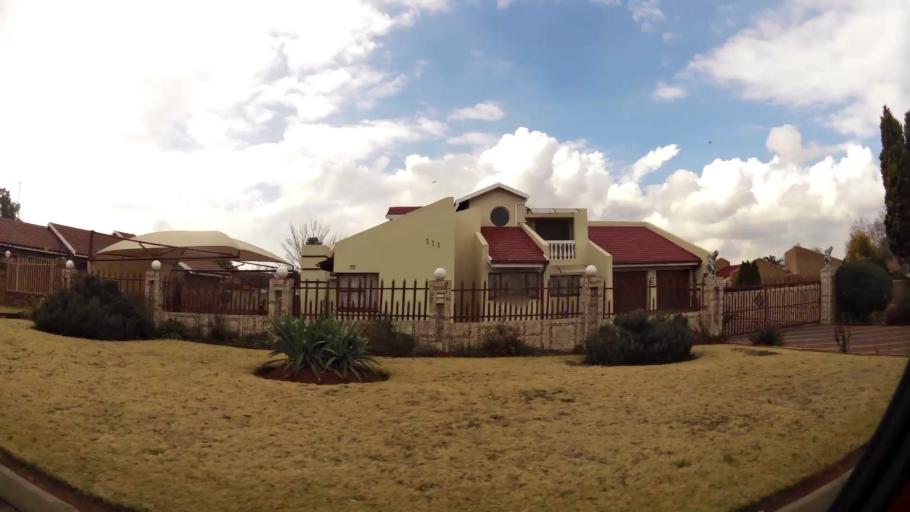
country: ZA
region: Gauteng
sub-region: Sedibeng District Municipality
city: Vanderbijlpark
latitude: -26.7336
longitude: 27.8543
